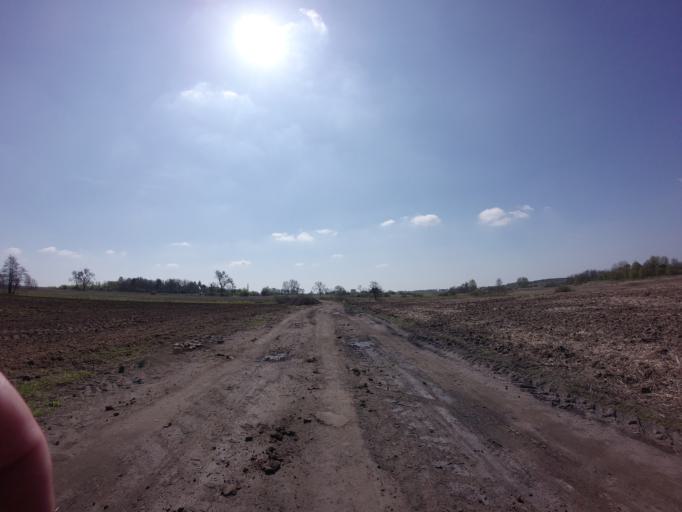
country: PL
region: West Pomeranian Voivodeship
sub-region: Powiat choszczenski
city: Choszczno
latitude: 53.1673
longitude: 15.4557
